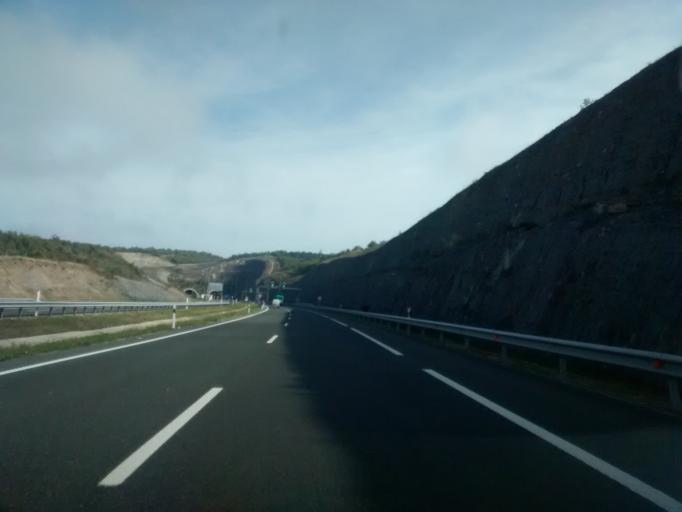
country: ES
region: Basque Country
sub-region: Provincia de Alava
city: Gasteiz / Vitoria
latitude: 42.9306
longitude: -2.6368
